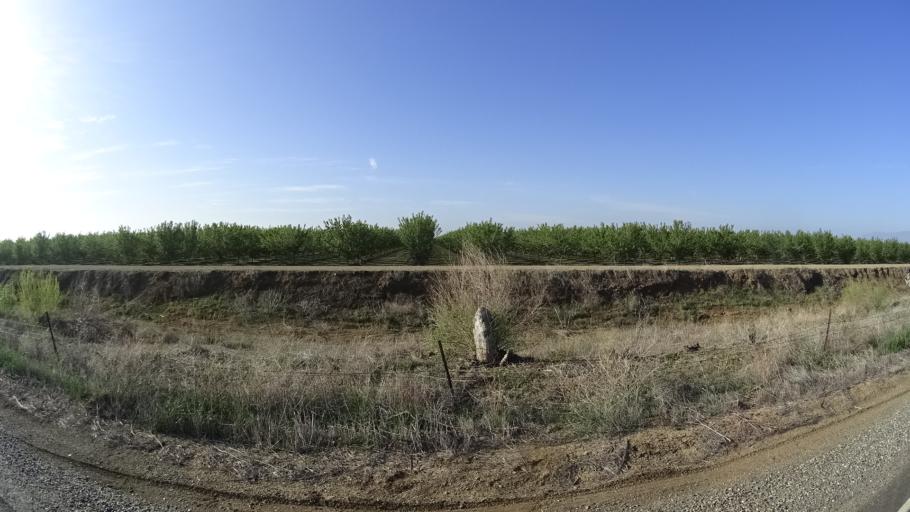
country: US
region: California
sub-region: Glenn County
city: Willows
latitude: 39.5824
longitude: -122.2447
